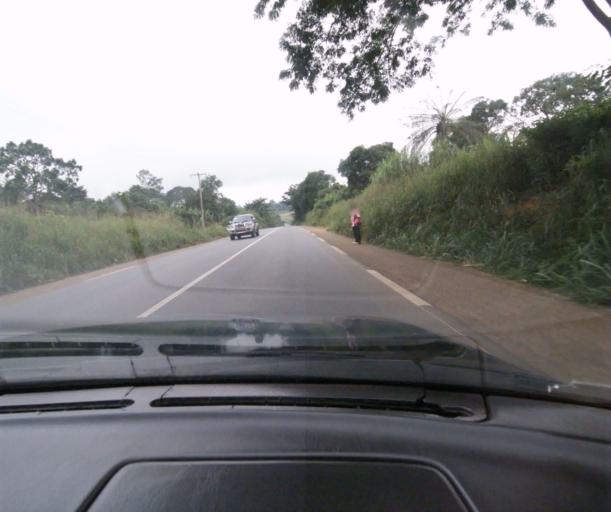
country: CM
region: Centre
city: Obala
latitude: 4.2221
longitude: 11.4339
